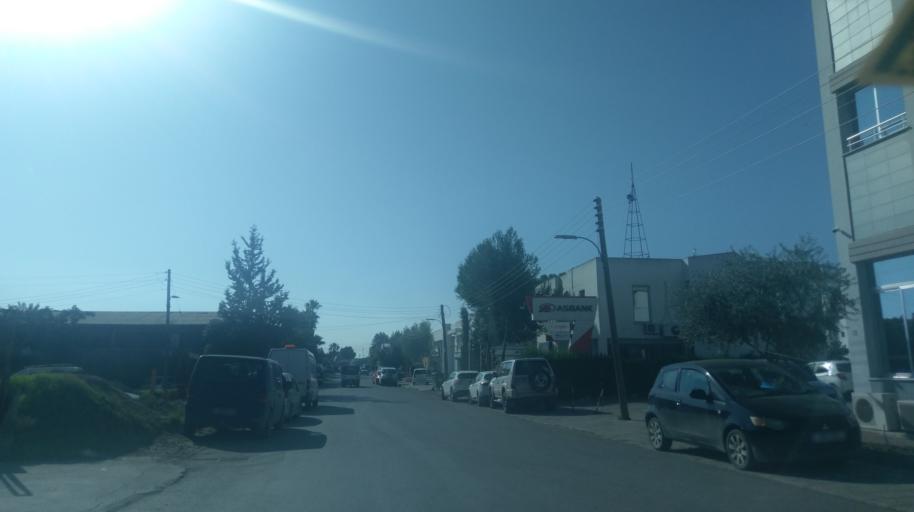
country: CY
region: Lefkosia
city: Nicosia
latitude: 35.2145
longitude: 33.3443
